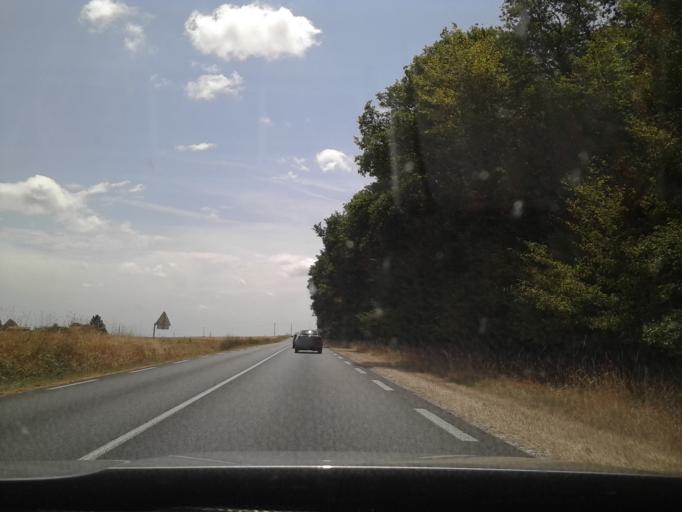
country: FR
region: Centre
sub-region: Departement d'Indre-et-Loire
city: Poce-sur-Cisse
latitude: 47.4976
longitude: 1.0052
